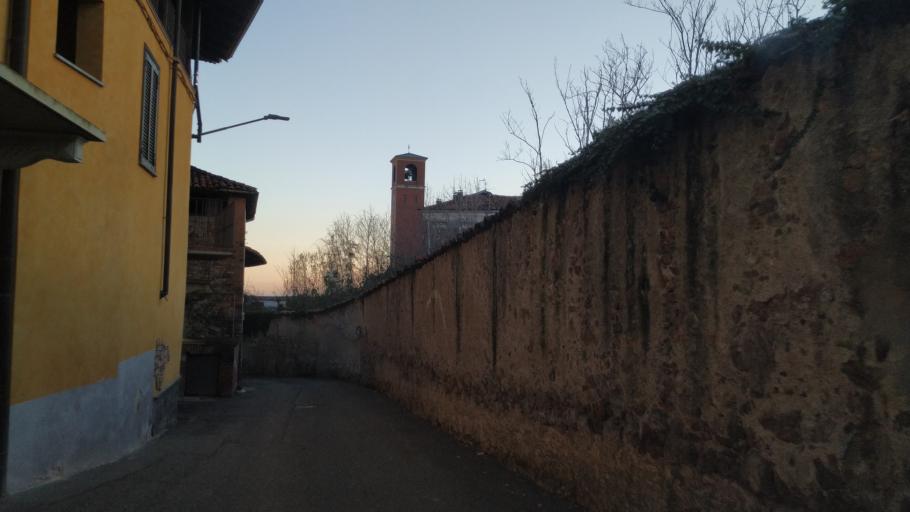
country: IT
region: Piedmont
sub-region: Provincia di Vercelli
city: Lozzolo
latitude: 45.6269
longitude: 8.3218
